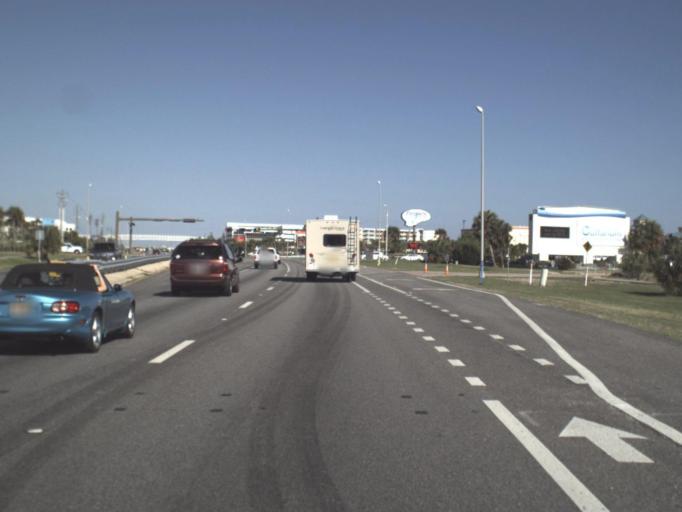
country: US
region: Florida
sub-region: Okaloosa County
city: Fort Walton Beach
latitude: 30.3962
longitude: -86.5947
